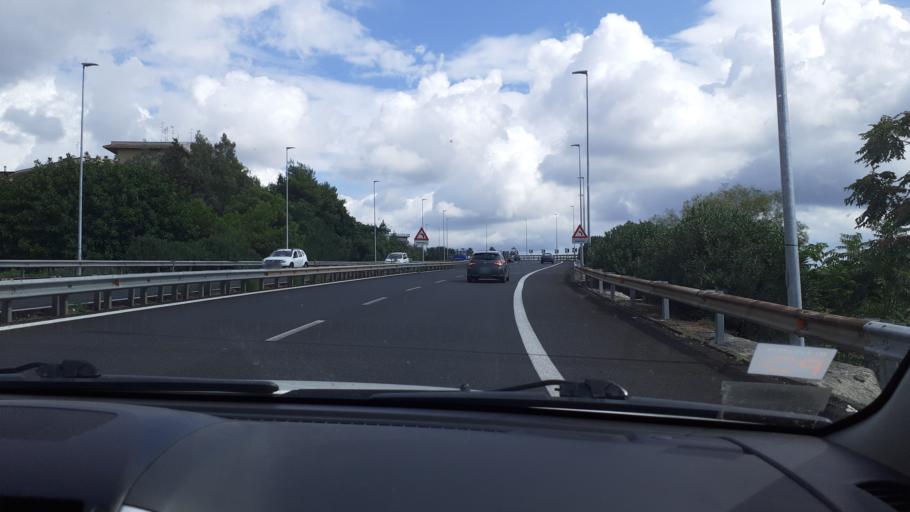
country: IT
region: Sicily
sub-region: Catania
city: Canalicchio
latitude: 37.5340
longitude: 15.0950
